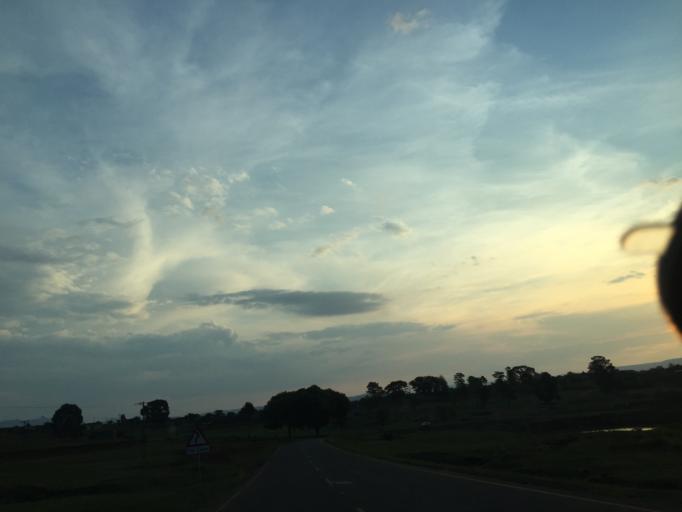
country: LS
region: Maseru
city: Nako
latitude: -29.4210
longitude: 27.7096
